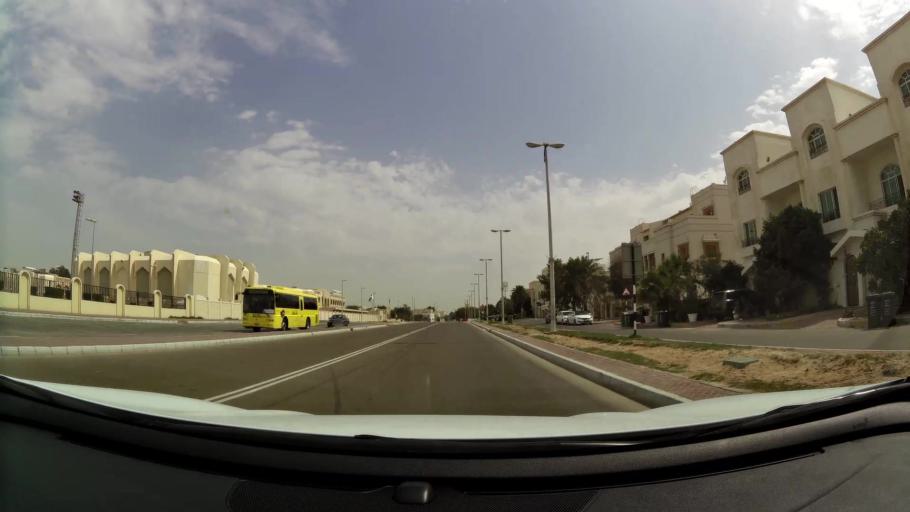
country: AE
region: Abu Dhabi
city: Abu Dhabi
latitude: 24.4608
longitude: 54.3431
